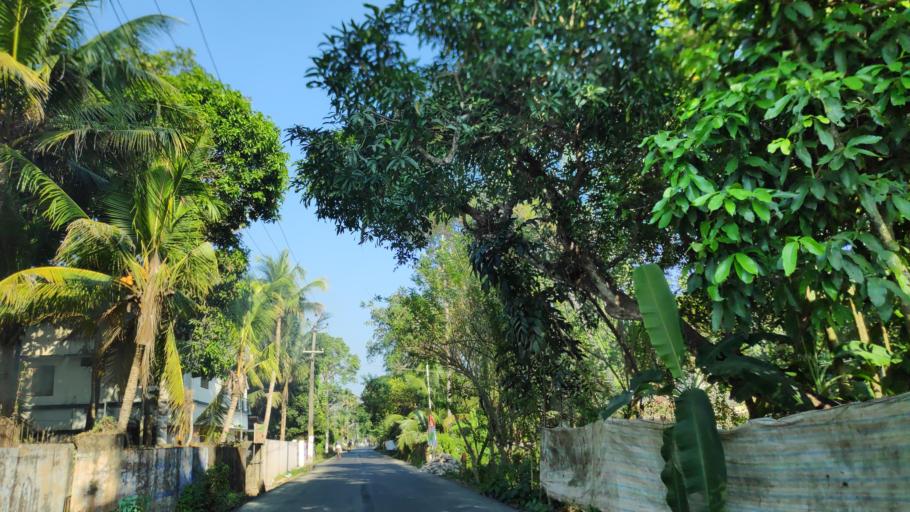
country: IN
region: Kerala
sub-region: Alappuzha
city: Alleppey
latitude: 9.5699
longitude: 76.3130
